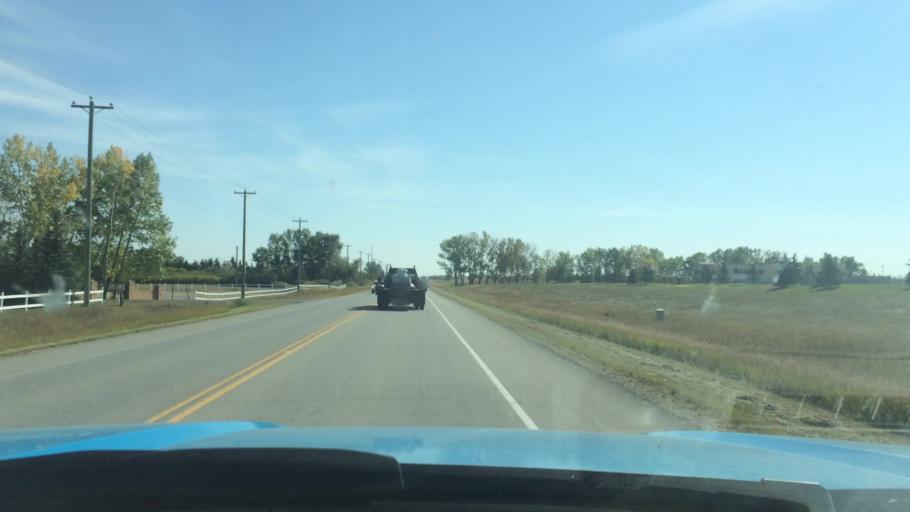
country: CA
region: Alberta
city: Airdrie
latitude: 51.2124
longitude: -113.9669
